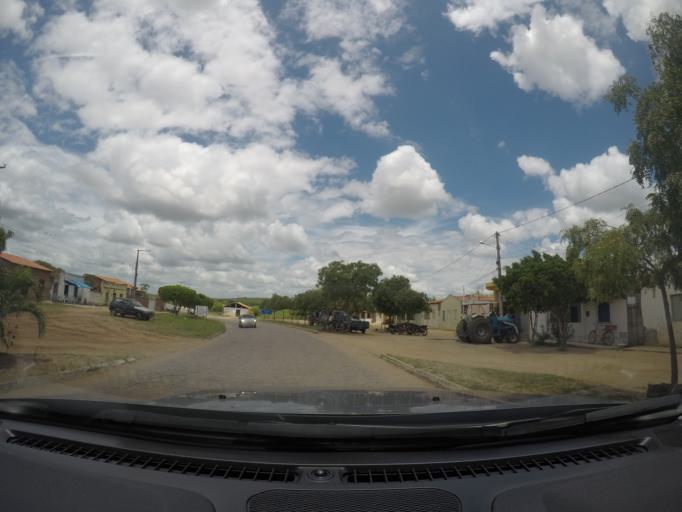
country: BR
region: Bahia
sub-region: Itaberaba
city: Itaberaba
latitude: -12.3616
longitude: -40.0390
